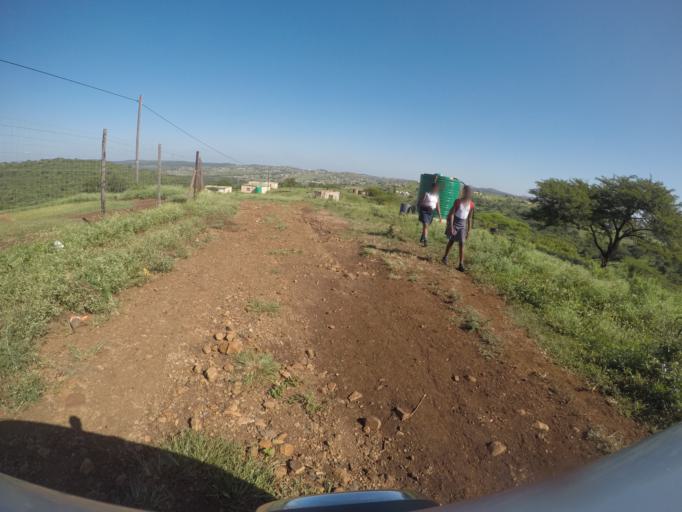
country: ZA
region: KwaZulu-Natal
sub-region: uThungulu District Municipality
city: Empangeni
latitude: -28.5743
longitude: 31.7317
